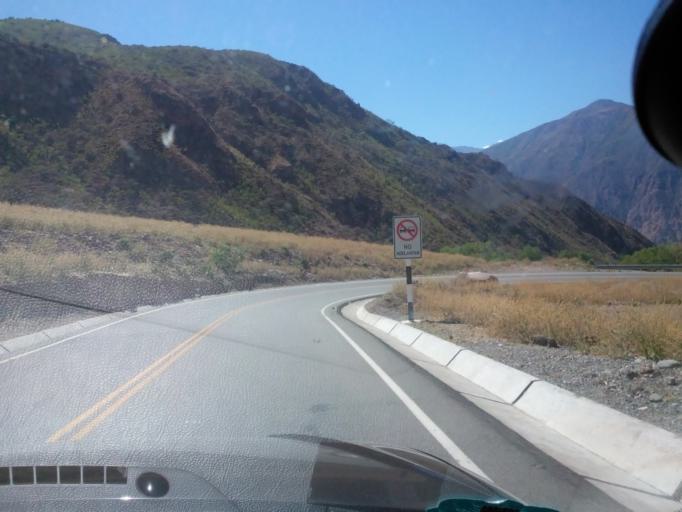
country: PE
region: Ayacucho
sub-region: Provincia de Huamanga
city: Ocros
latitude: -13.4228
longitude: -73.8658
